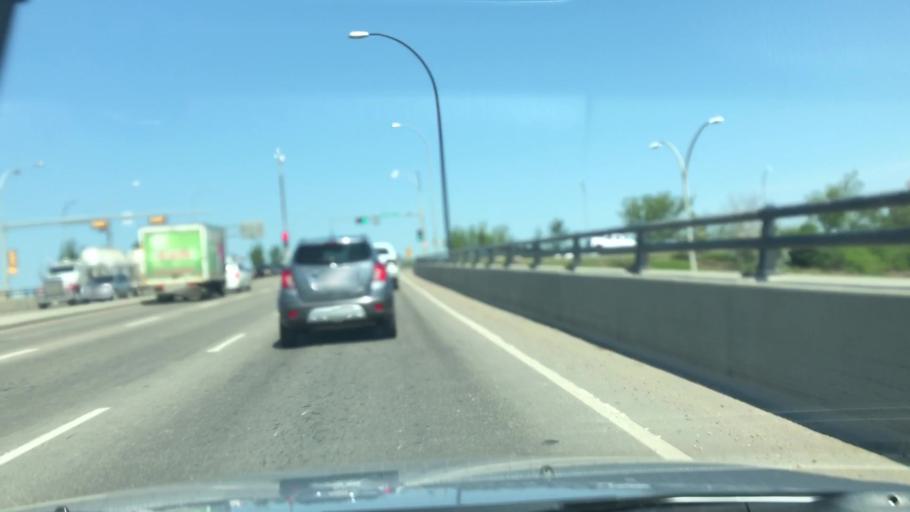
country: CA
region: Alberta
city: St. Albert
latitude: 53.5789
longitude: -113.5907
